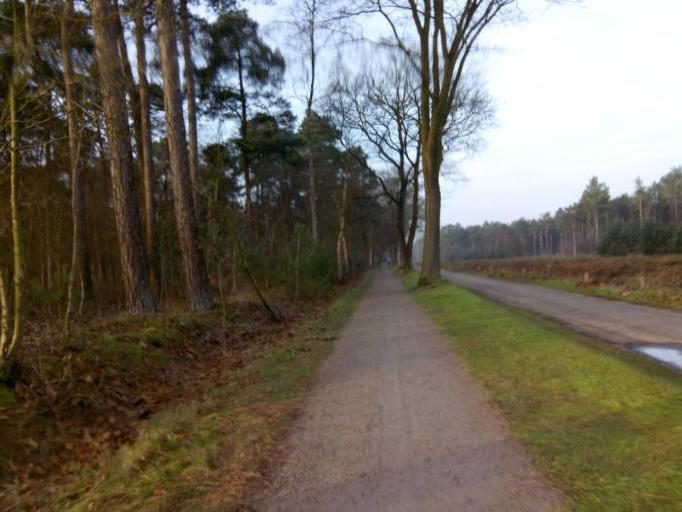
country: NL
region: Utrecht
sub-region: Gemeente Amersfoort
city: Amersfoort
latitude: 52.1184
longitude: 5.3758
